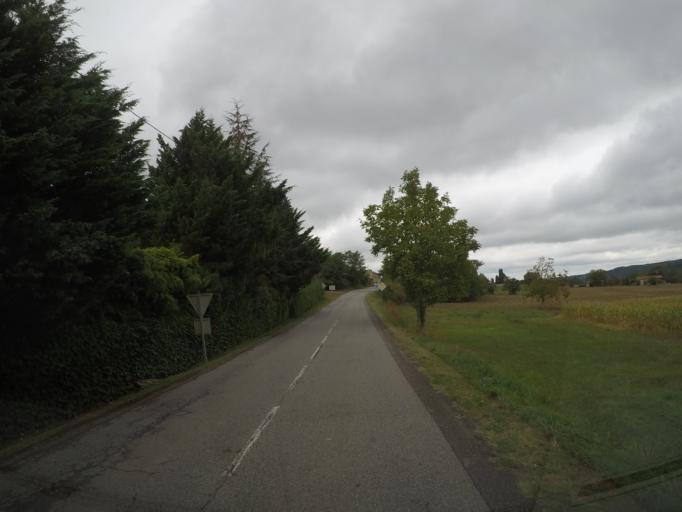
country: FR
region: Midi-Pyrenees
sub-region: Departement de la Haute-Garonne
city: Gaillac-Toulza
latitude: 43.1041
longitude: 1.4411
